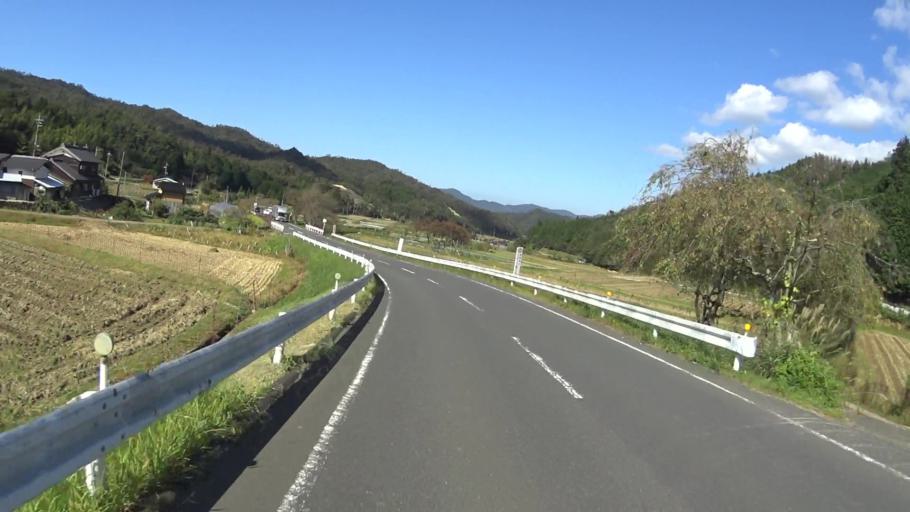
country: JP
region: Hyogo
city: Toyooka
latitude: 35.5475
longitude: 134.9784
